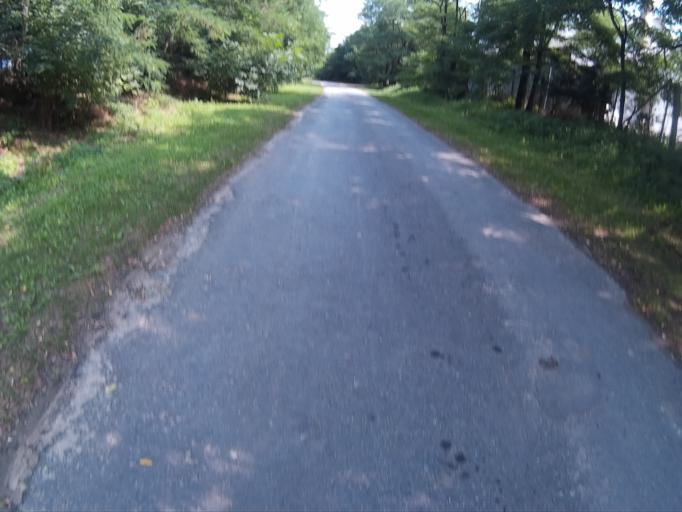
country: HU
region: Veszprem
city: Papa
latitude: 47.2879
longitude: 17.5786
